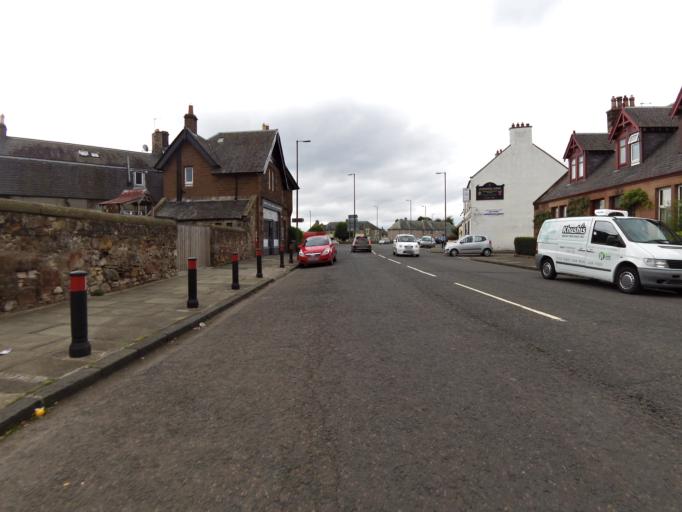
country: GB
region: Scotland
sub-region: East Lothian
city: Musselburgh
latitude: 55.9450
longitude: -3.0252
